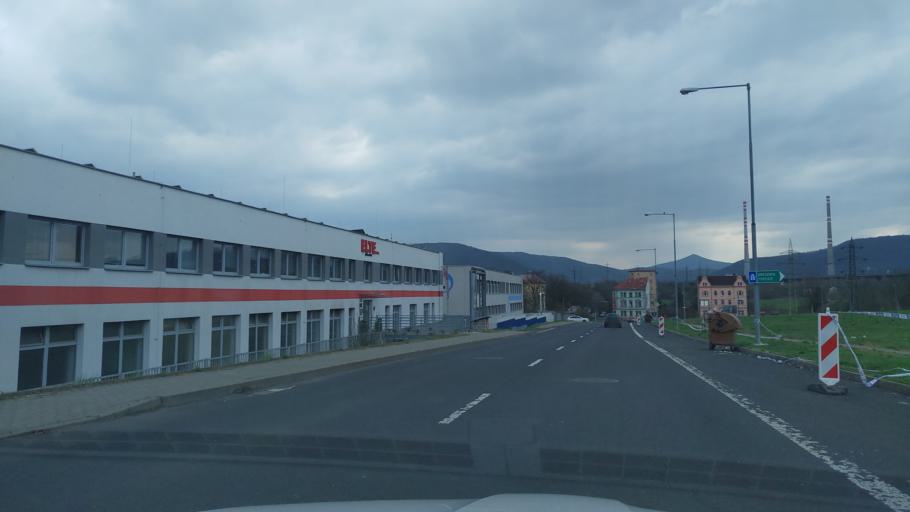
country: CZ
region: Ustecky
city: Trmice
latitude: 50.6599
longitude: 13.9943
